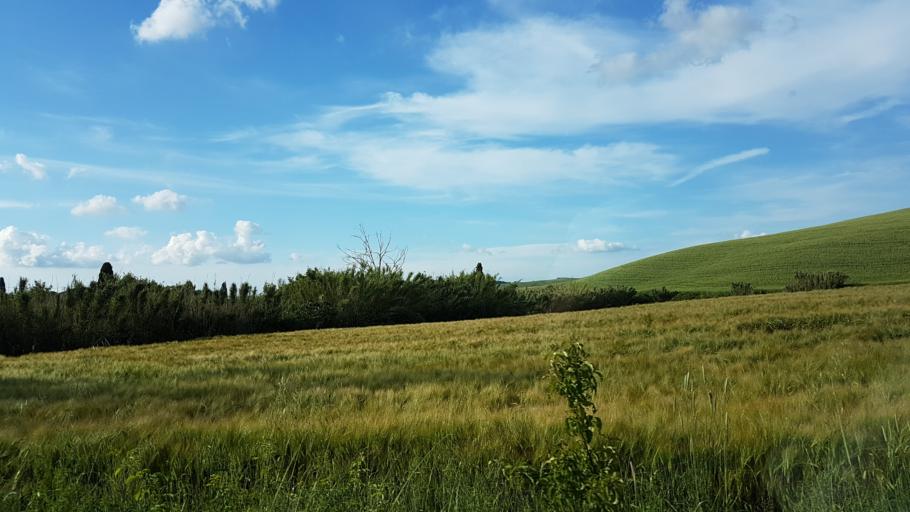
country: IT
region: Tuscany
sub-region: Province of Pisa
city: Chianni
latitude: 43.4849
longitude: 10.6691
